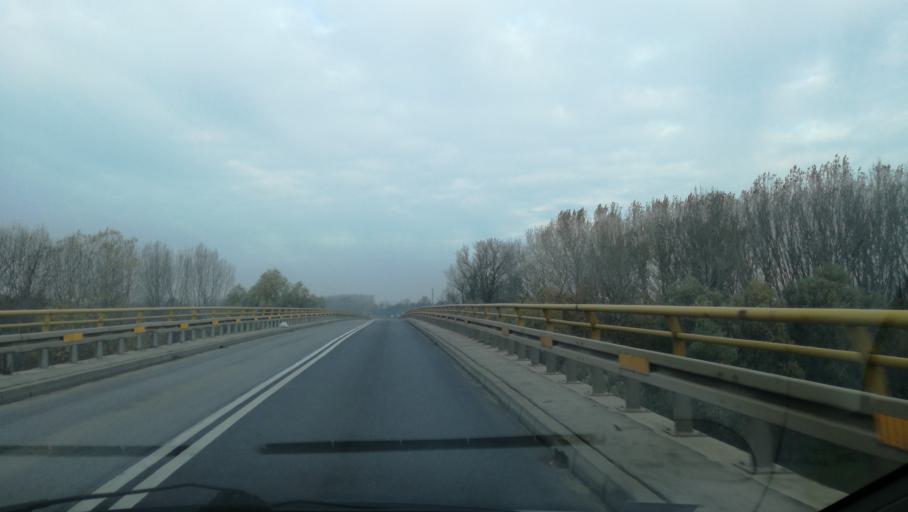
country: RS
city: Taras
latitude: 45.3978
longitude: 20.2119
